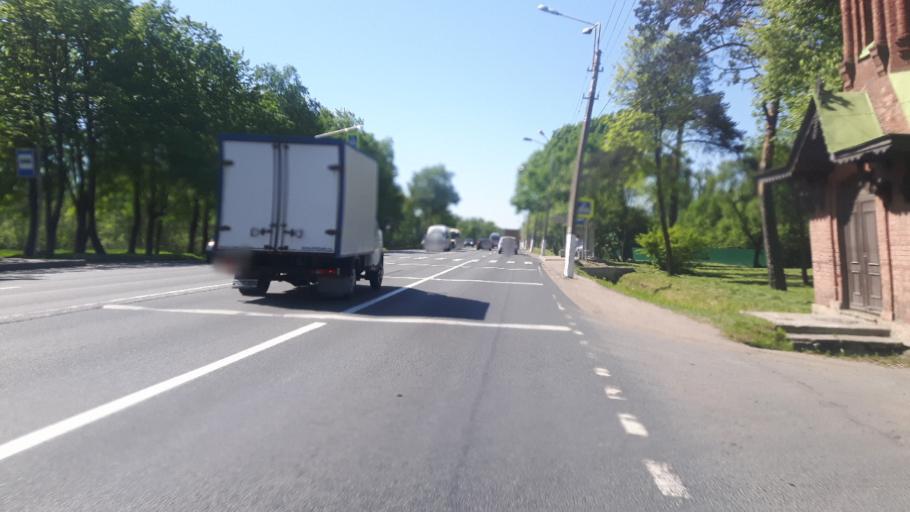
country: RU
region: Leningrad
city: Ol'gino
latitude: 59.8728
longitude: 29.9599
